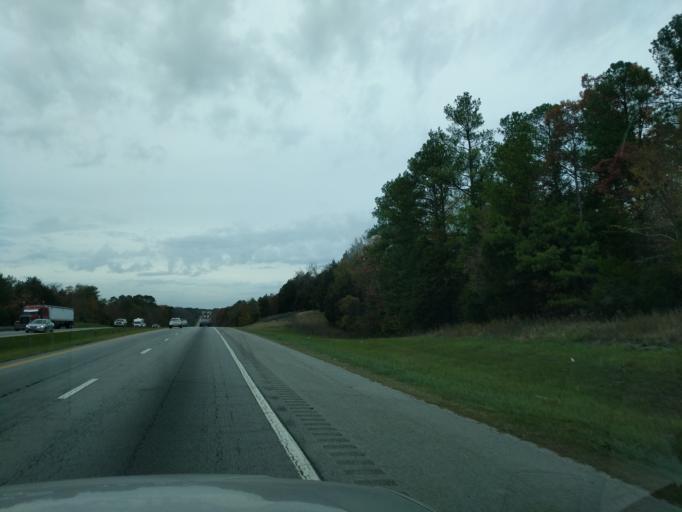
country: US
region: South Carolina
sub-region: Newberry County
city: Newberry
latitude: 34.3501
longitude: -81.6423
